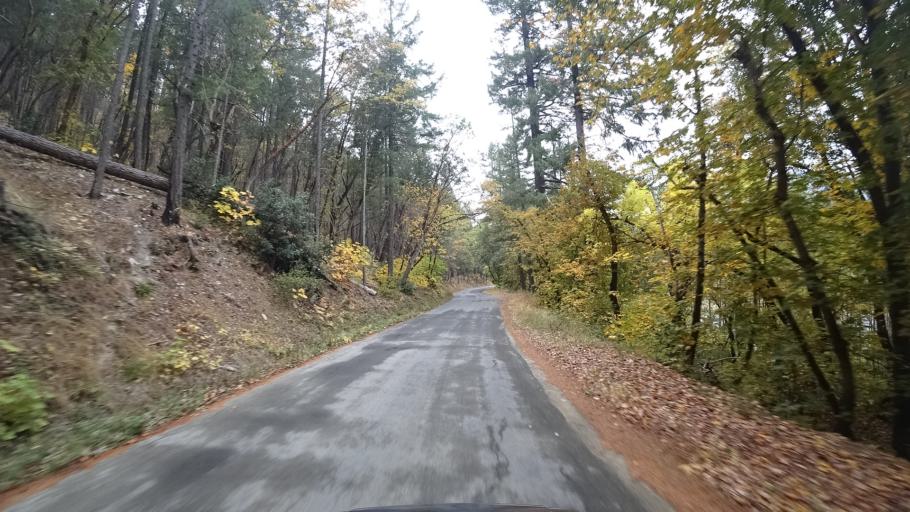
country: US
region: California
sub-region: Siskiyou County
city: Happy Camp
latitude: 41.8257
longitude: -123.1882
